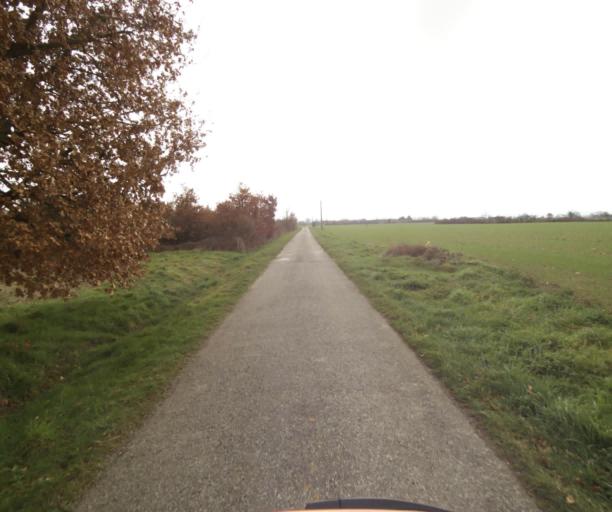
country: FR
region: Midi-Pyrenees
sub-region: Departement de l'Ariege
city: La Tour-du-Crieu
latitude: 43.1686
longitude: 1.6859
